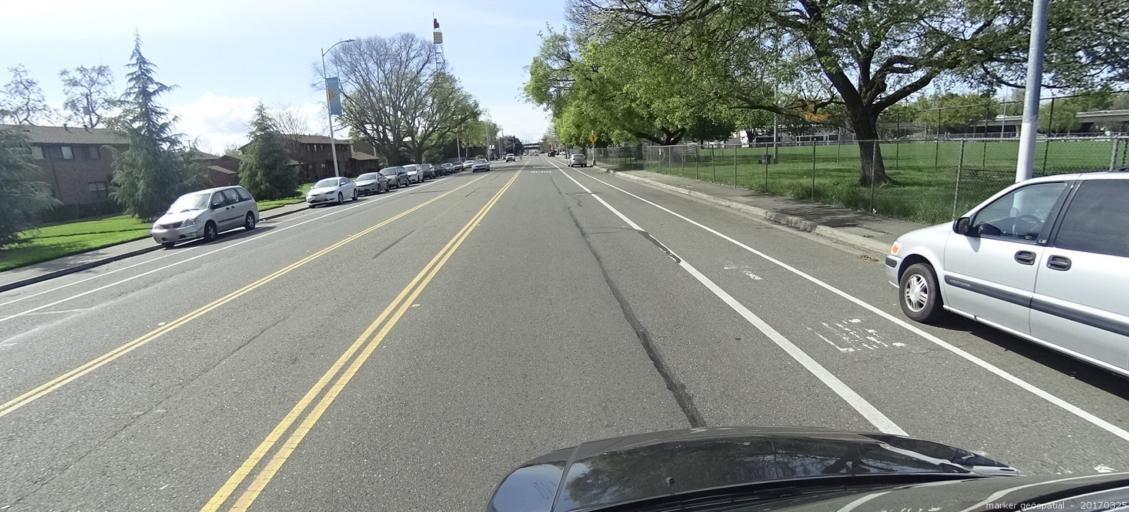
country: US
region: California
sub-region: Sacramento County
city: Sacramento
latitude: 38.5647
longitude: -121.5040
